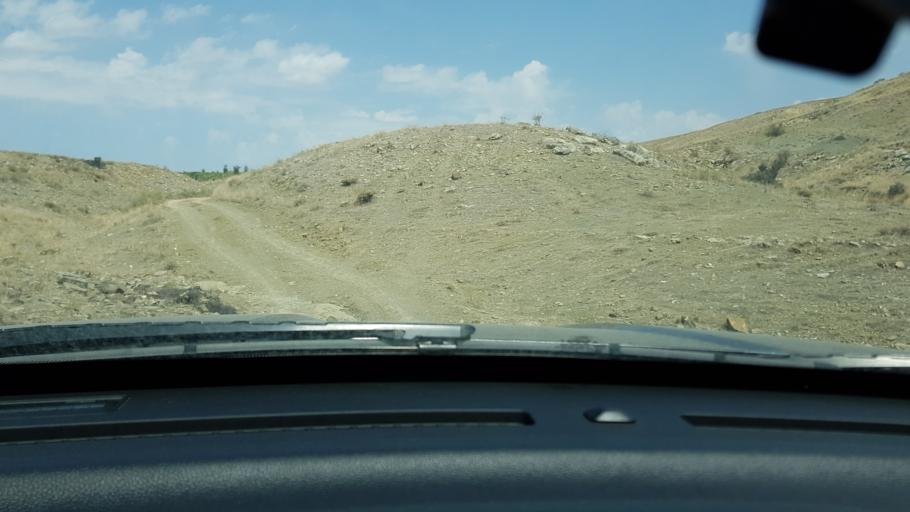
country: TM
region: Ahal
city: Baharly
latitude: 38.4061
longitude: 56.9094
